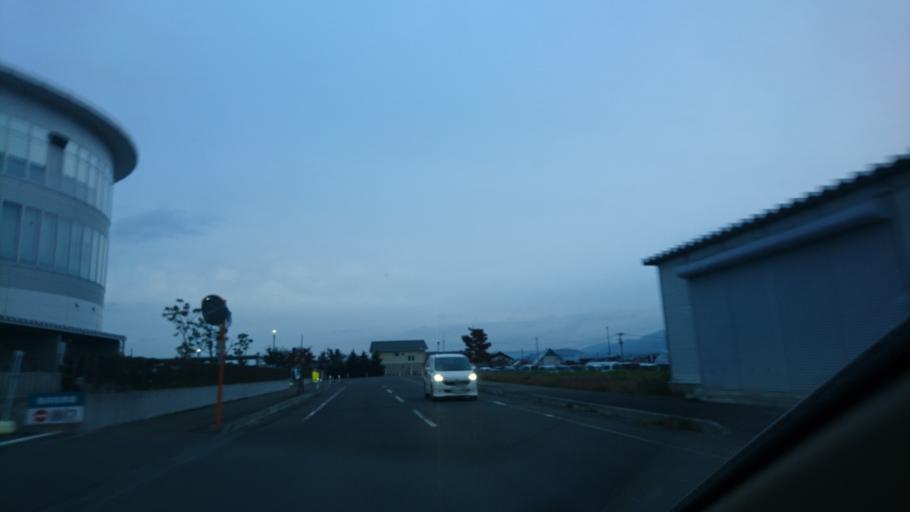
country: JP
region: Iwate
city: Morioka-shi
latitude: 39.6704
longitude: 141.1319
